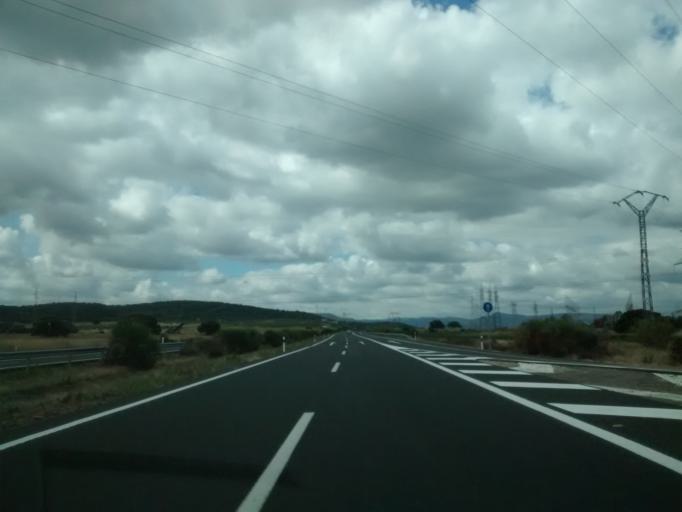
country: ES
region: Extremadura
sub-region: Provincia de Caceres
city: Almaraz
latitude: 39.8250
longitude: -5.6598
